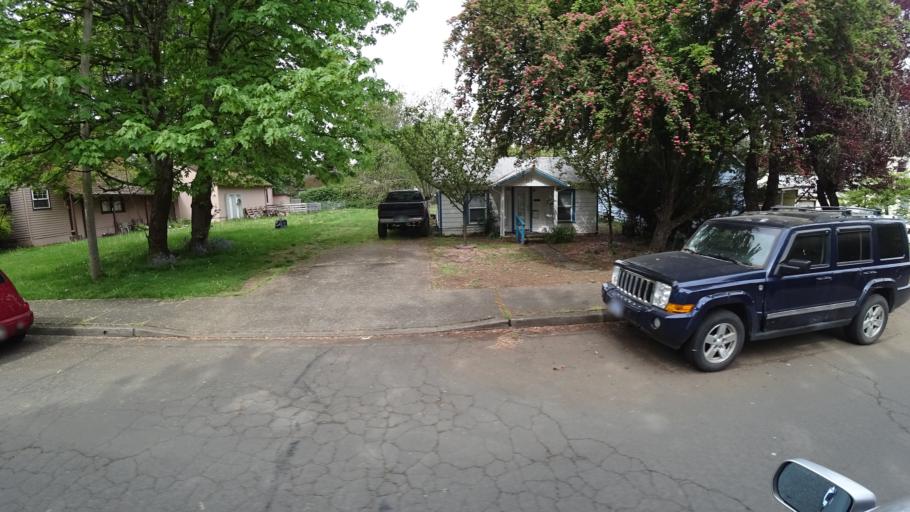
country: US
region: Oregon
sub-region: Washington County
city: Hillsboro
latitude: 45.5231
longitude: -122.9974
